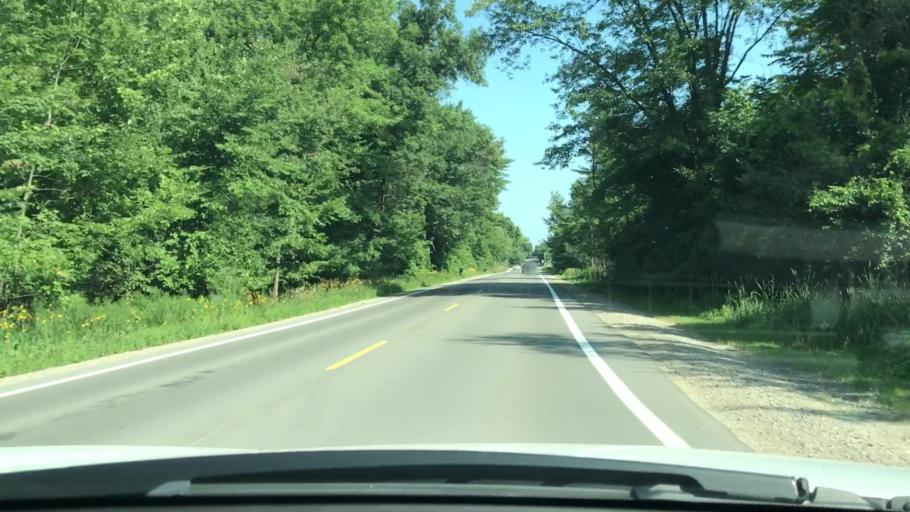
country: US
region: Michigan
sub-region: Oakland County
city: Oxford
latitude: 42.7926
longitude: -83.3329
